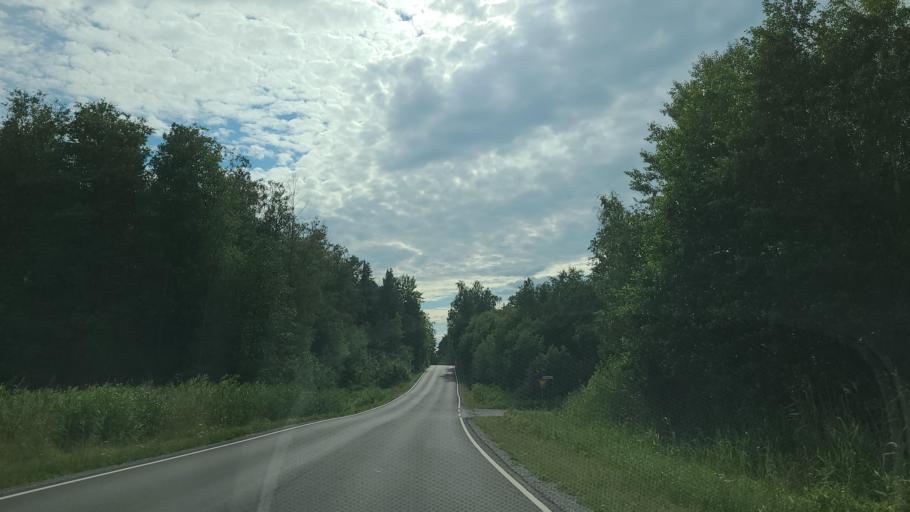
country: FI
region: Varsinais-Suomi
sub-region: Turku
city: Rymaettylae
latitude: 60.3314
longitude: 21.9771
